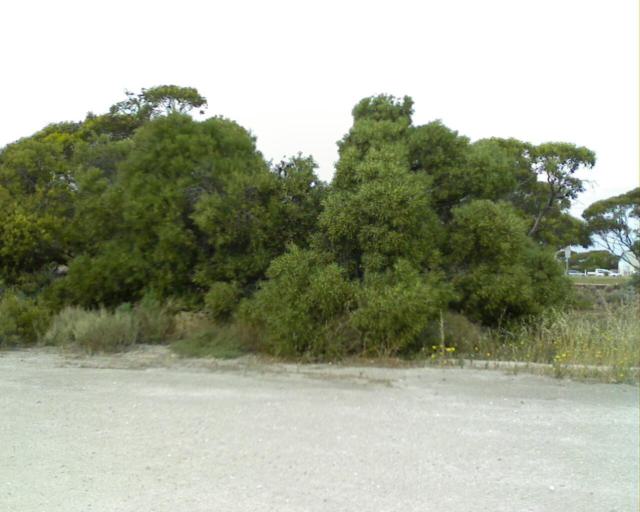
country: AU
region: South Australia
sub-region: Ceduna
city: Ceduna
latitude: -31.9274
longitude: 133.0069
